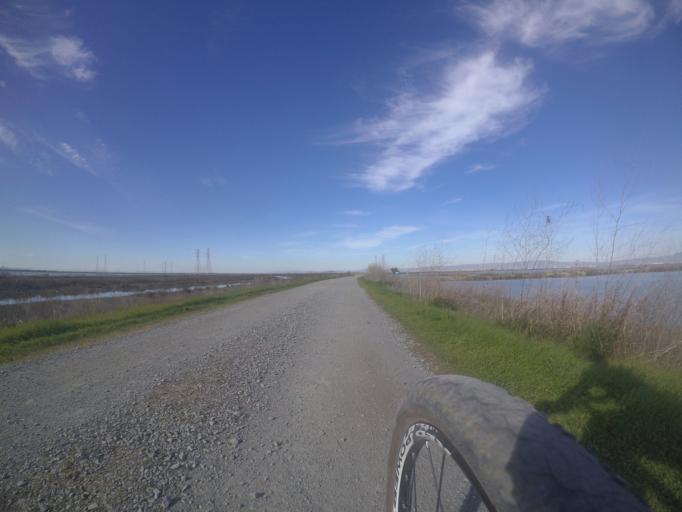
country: US
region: California
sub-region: Santa Clara County
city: Mountain View
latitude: 37.4381
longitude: -122.0679
